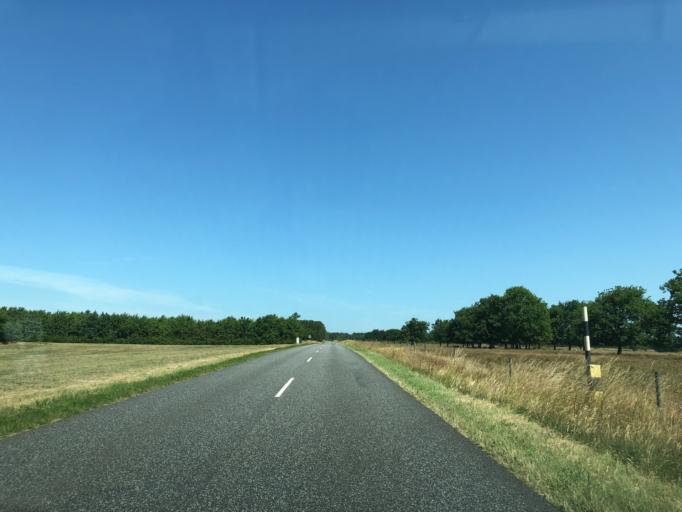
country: DK
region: Central Jutland
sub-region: Skive Kommune
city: Skive
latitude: 56.5239
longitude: 9.0320
